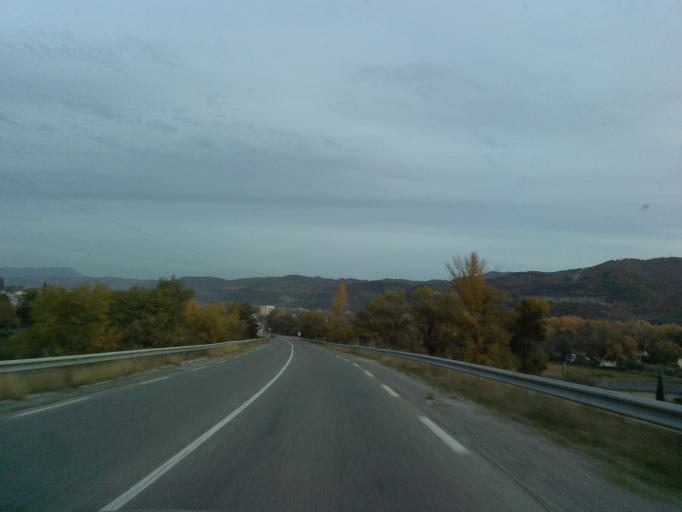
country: FR
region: Provence-Alpes-Cote d'Azur
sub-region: Departement des Alpes-de-Haute-Provence
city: Malijai
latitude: 44.0538
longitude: 6.0205
